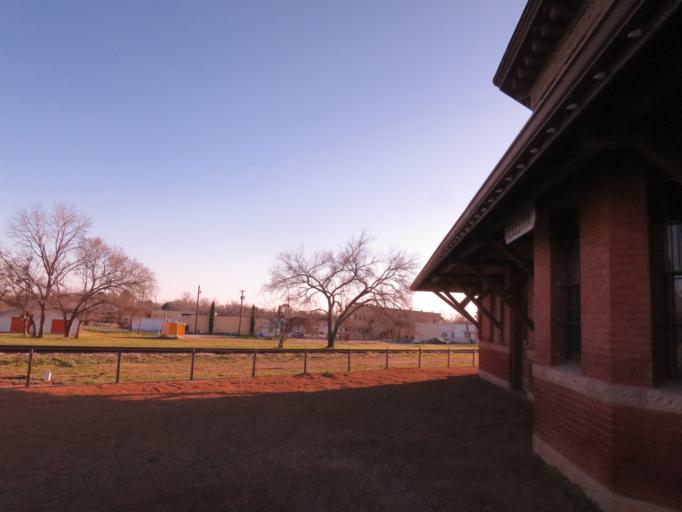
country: US
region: Texas
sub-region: Bastrop County
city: Elgin
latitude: 30.3477
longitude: -97.3695
